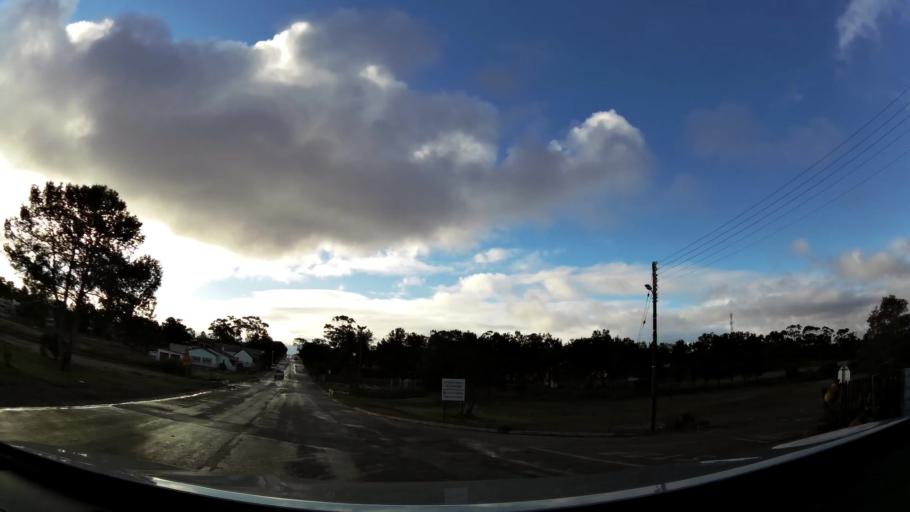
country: ZA
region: Western Cape
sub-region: Eden District Municipality
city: Riversdale
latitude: -34.2018
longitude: 21.5851
